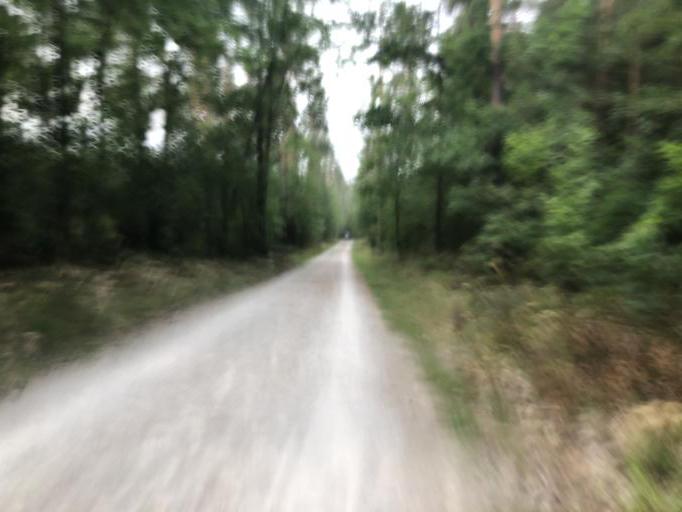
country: DE
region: Bavaria
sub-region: Regierungsbezirk Mittelfranken
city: Erlangen
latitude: 49.5612
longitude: 11.0303
